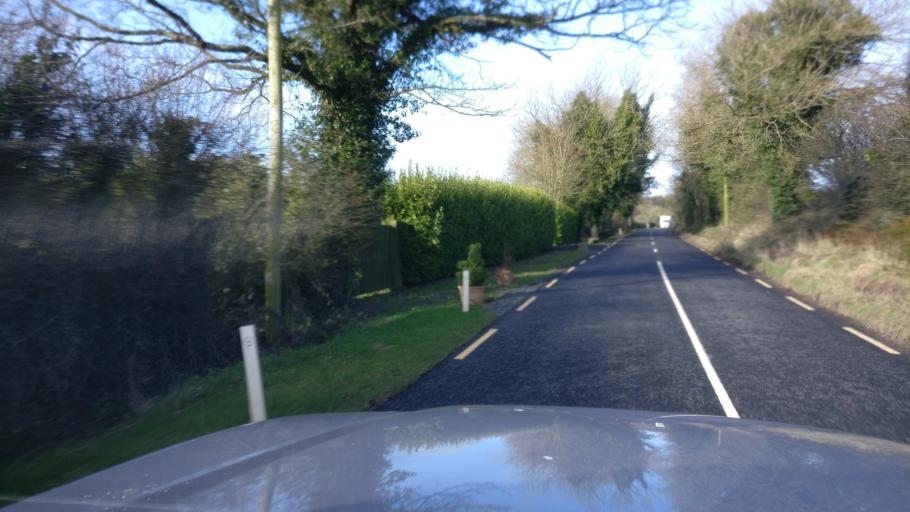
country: IE
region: Leinster
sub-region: Kilkenny
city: Castlecomer
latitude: 52.9069
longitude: -7.1828
